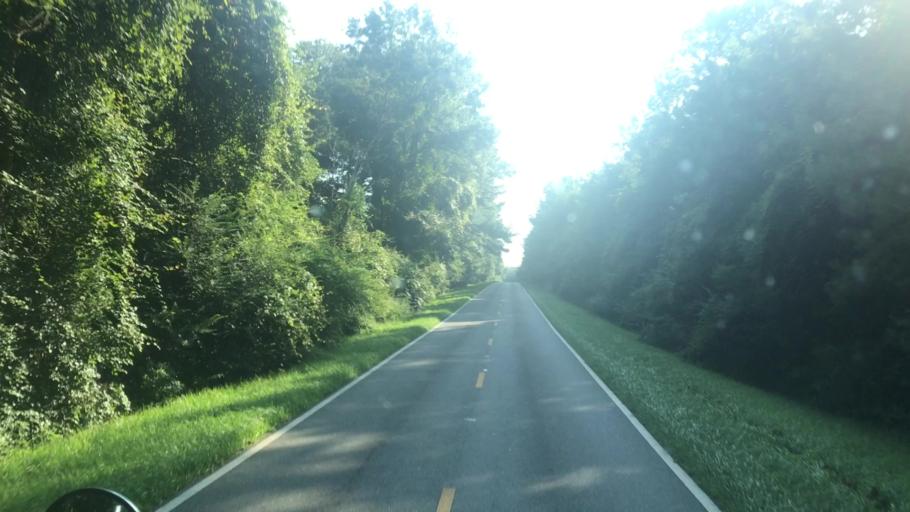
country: US
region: Florida
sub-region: Gadsden County
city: Quincy
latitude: 30.6696
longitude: -84.5480
